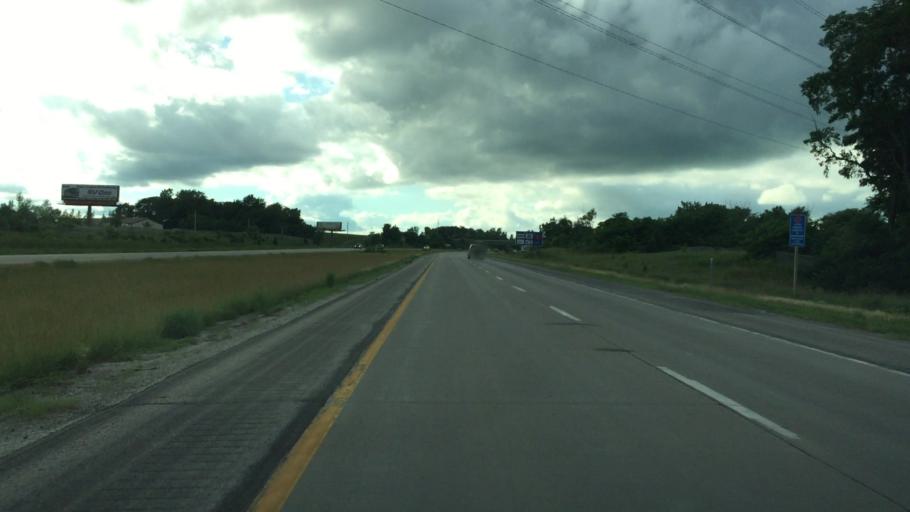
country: US
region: Iowa
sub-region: Polk County
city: Altoona
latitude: 41.6270
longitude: -93.4979
